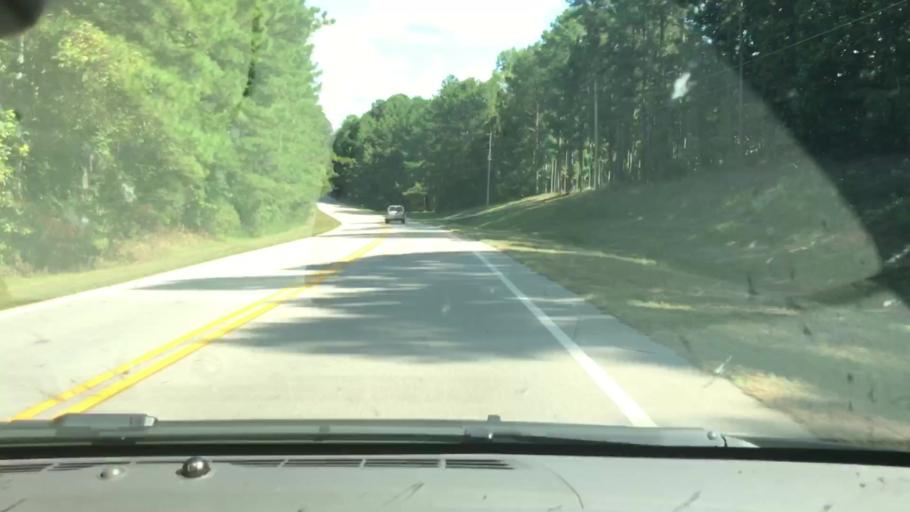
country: US
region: Georgia
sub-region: Troup County
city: La Grange
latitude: 33.1025
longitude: -85.0716
